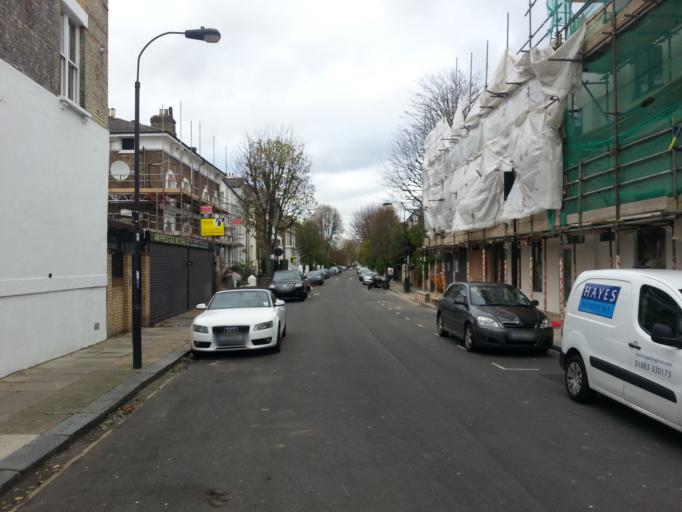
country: GB
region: England
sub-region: Greater London
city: Hammersmith
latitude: 51.5015
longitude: -0.2318
